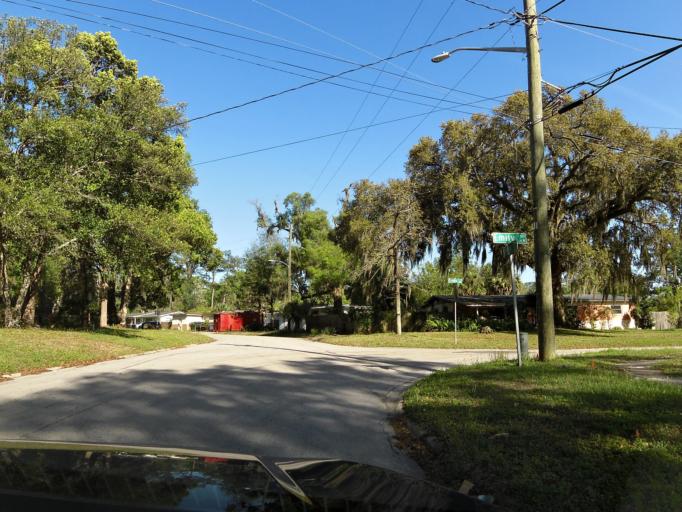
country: US
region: Florida
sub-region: Duval County
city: Jacksonville
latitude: 30.2765
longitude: -81.5855
